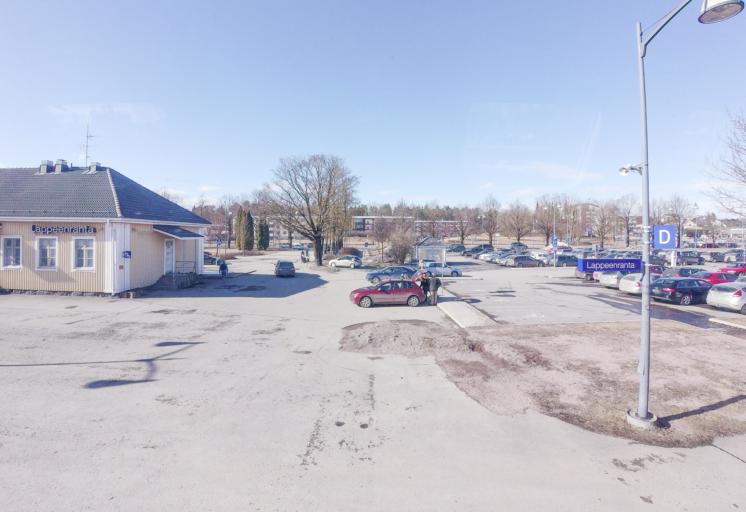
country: FI
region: South Karelia
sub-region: Lappeenranta
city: Lappeenranta
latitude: 61.0480
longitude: 28.1954
